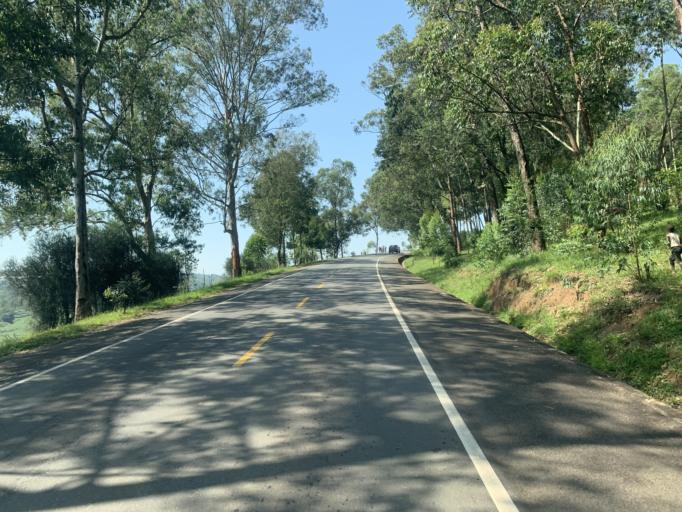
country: RW
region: Kigali
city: Kigali
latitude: -1.9932
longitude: 29.9277
